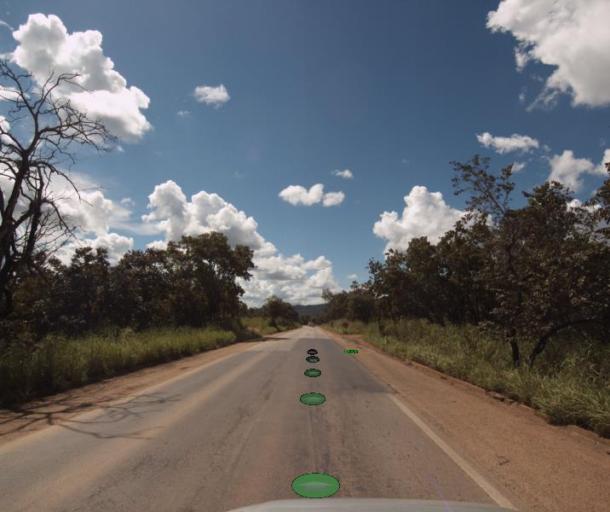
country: BR
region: Goias
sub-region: Porangatu
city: Porangatu
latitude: -13.6840
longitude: -49.0232
